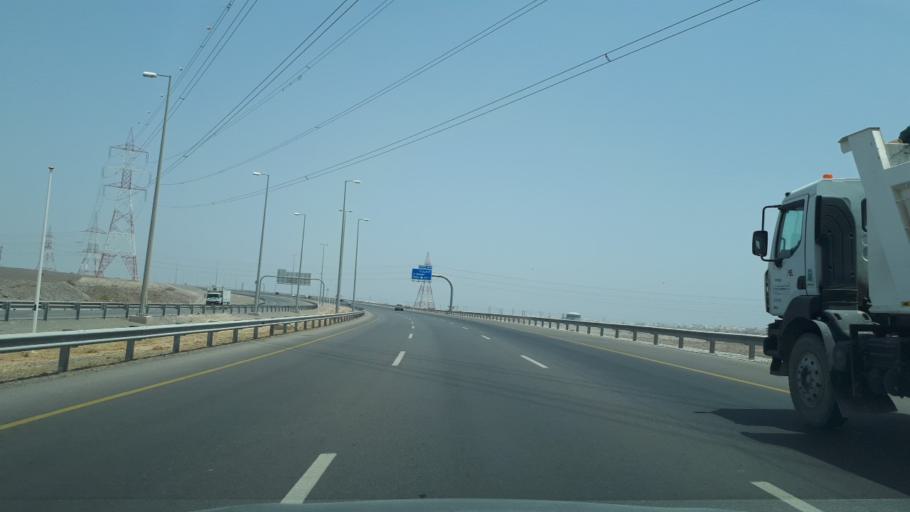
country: OM
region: Muhafazat Masqat
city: As Sib al Jadidah
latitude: 23.6206
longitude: 58.0884
